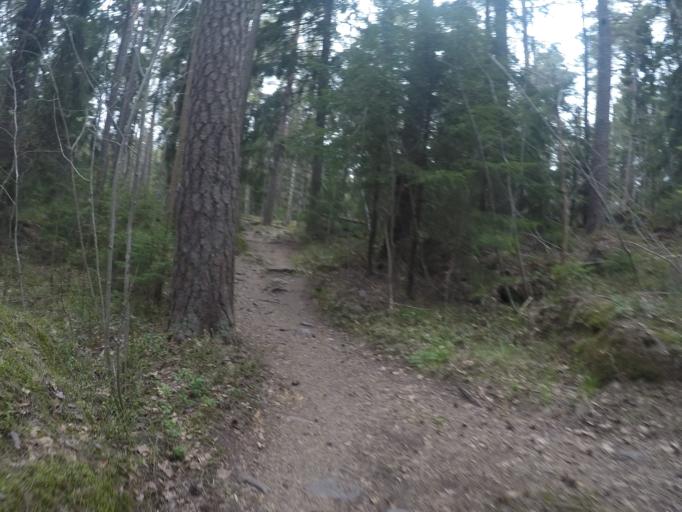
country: SE
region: Vaestmanland
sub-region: Vasteras
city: Vasteras
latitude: 59.6283
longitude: 16.5258
